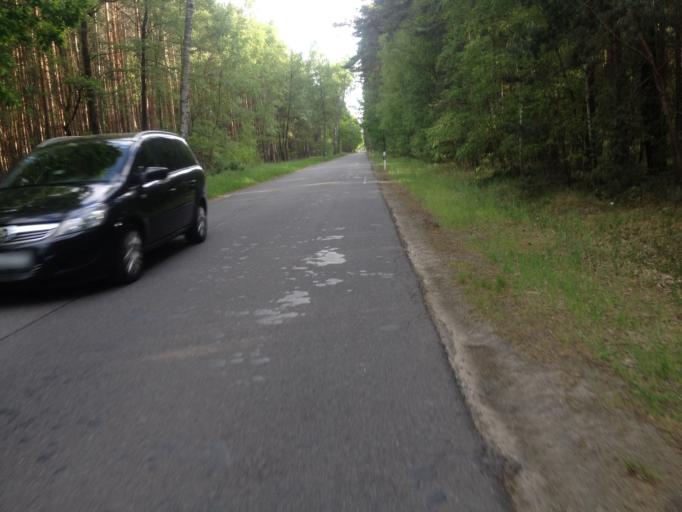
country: DE
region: Brandenburg
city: Cottbus
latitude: 51.8094
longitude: 14.3149
